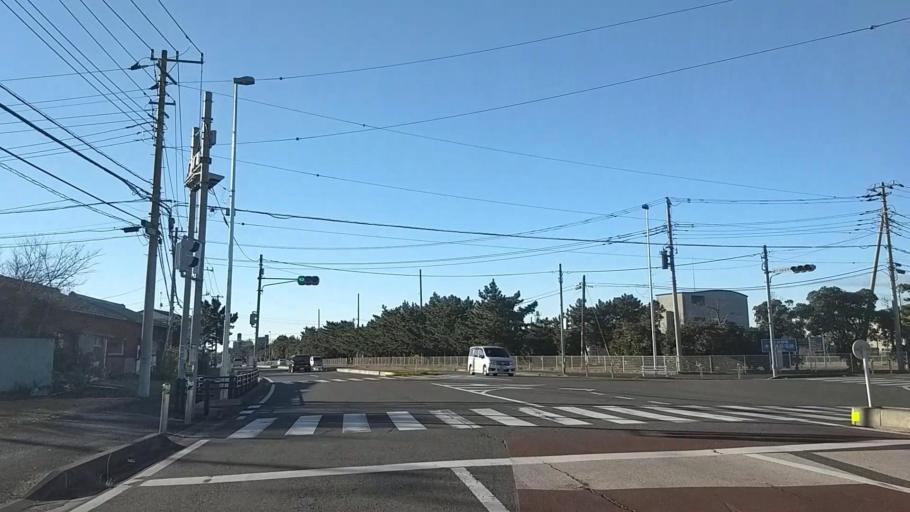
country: JP
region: Chiba
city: Kisarazu
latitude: 35.3927
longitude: 139.9194
